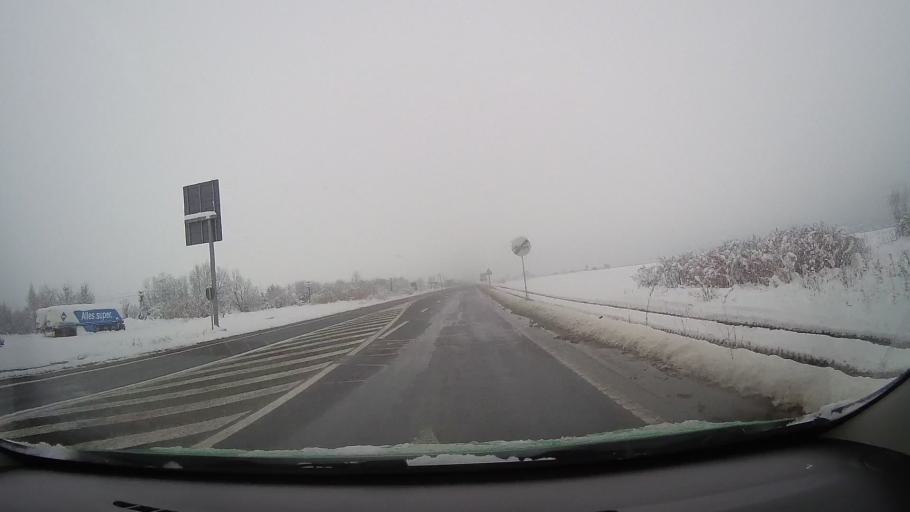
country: RO
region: Sibiu
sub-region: Oras Saliste
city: Saliste
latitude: 45.7996
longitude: 23.9019
